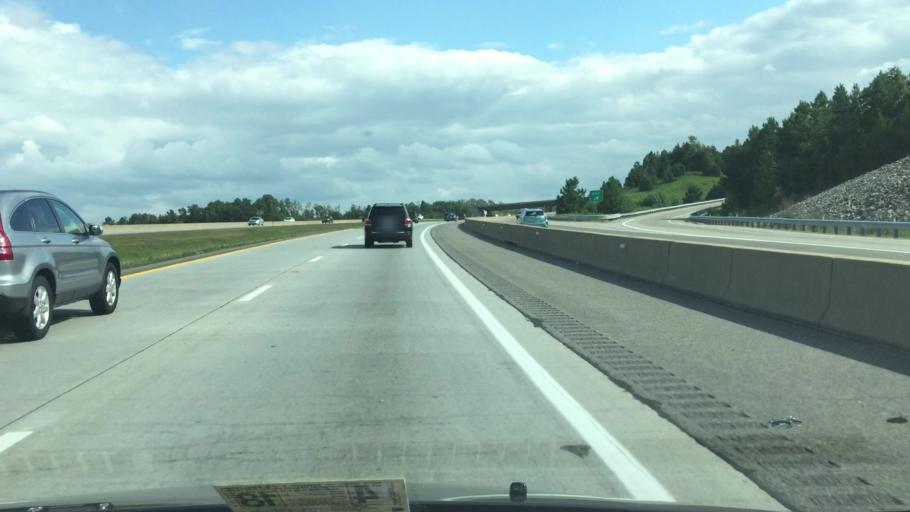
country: US
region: Virginia
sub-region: Chesterfield County
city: Brandermill
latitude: 37.5153
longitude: -77.6880
